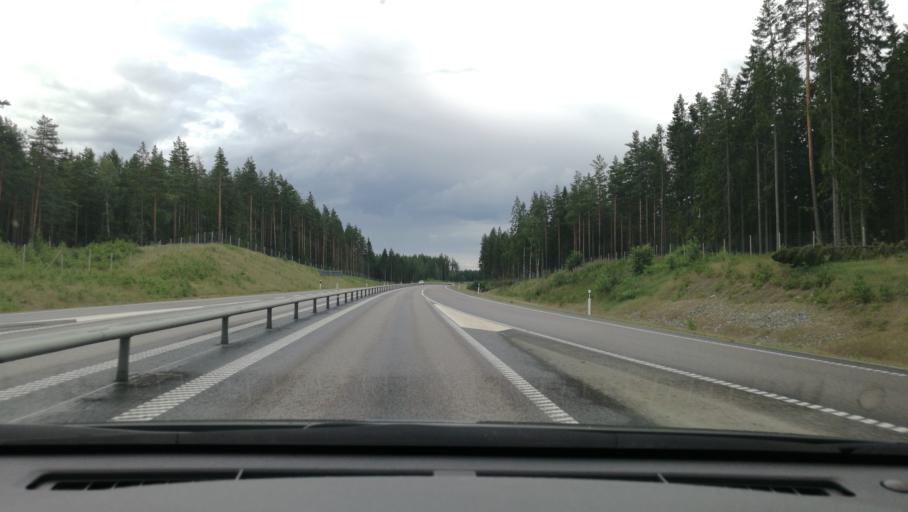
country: SE
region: Soedermanland
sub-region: Katrineholms Kommun
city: Katrineholm
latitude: 58.9925
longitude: 16.2611
